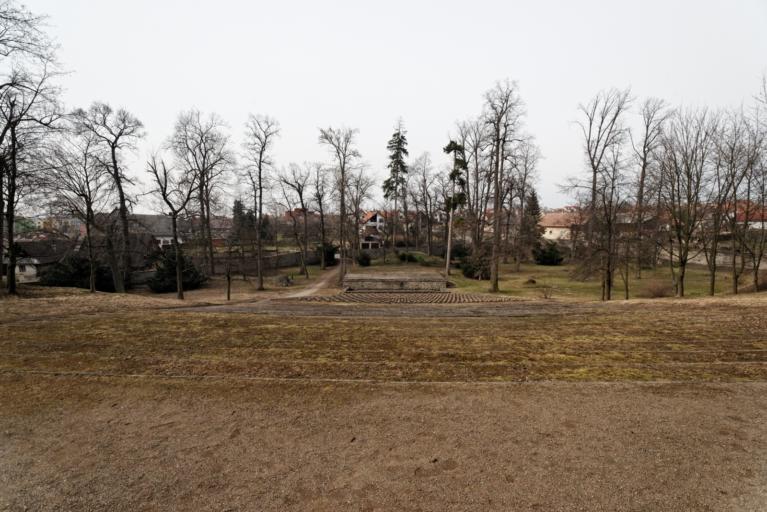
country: CZ
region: Pardubicky
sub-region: Okres Svitavy
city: Litomysl
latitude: 49.8737
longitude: 16.3126
